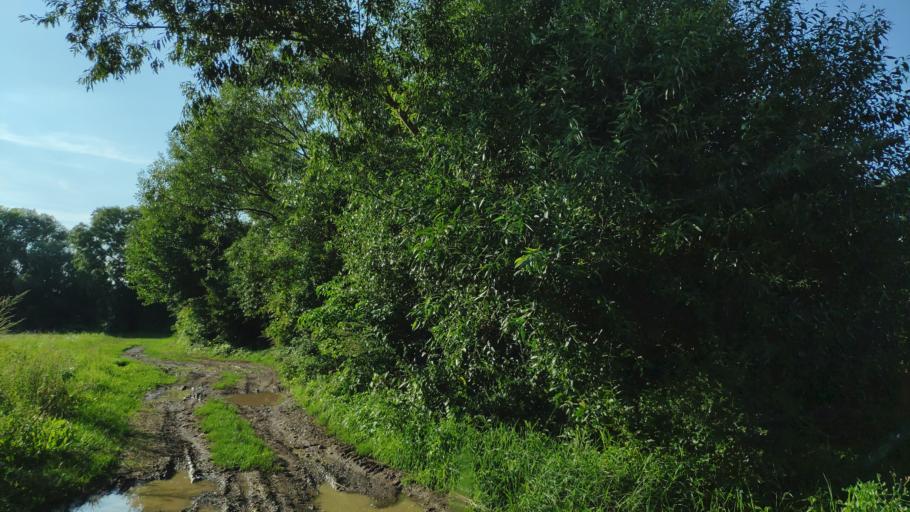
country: SK
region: Kosicky
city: Secovce
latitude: 48.6118
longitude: 21.5392
